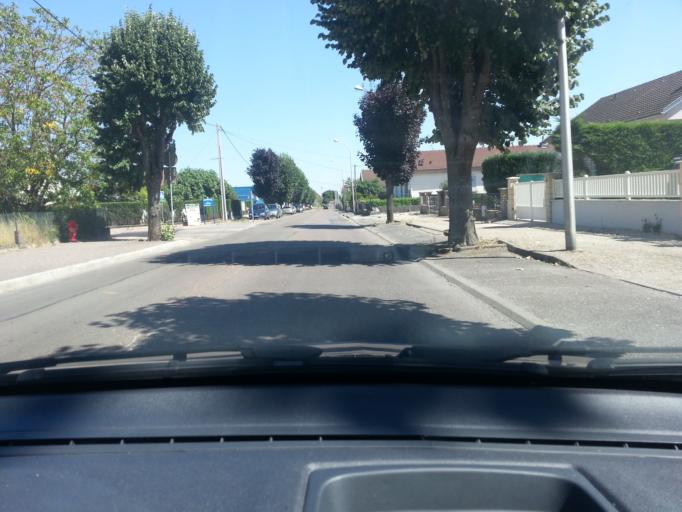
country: FR
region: Bourgogne
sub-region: Departement de la Cote-d'Or
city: Perrigny-les-Dijon
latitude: 47.2785
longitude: 5.0098
